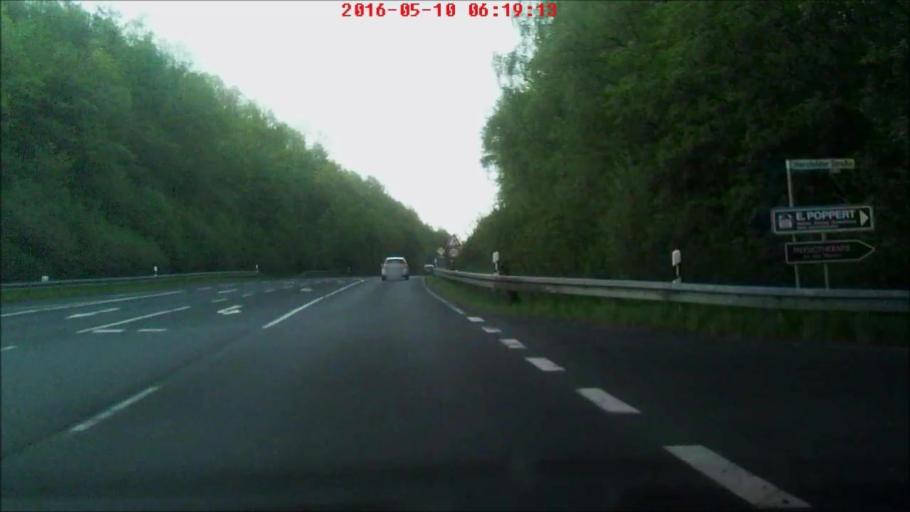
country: DE
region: Hesse
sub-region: Regierungsbezirk Kassel
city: Burghaun
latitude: 50.7139
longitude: 9.7180
